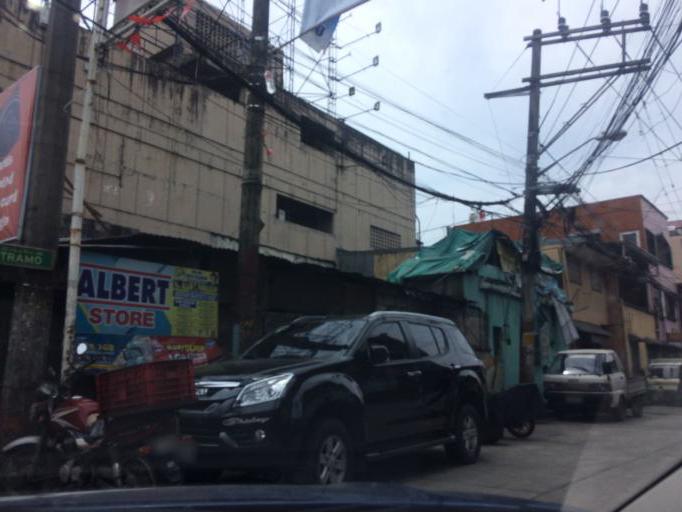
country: PH
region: Metro Manila
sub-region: Makati City
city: Makati City
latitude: 14.5380
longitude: 121.0032
